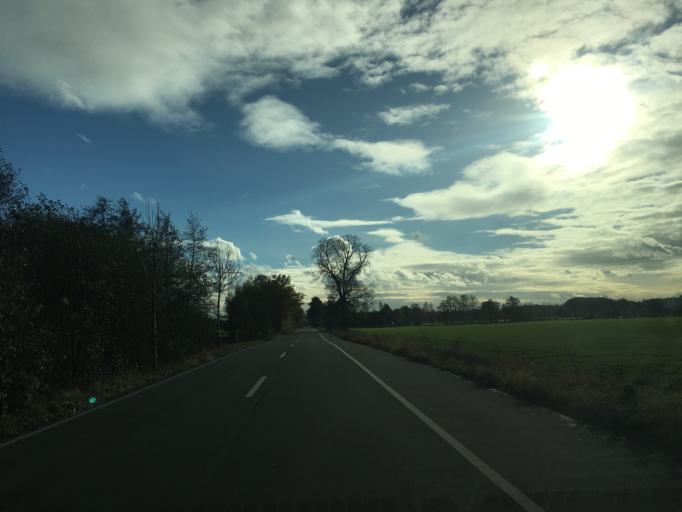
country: DE
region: North Rhine-Westphalia
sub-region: Regierungsbezirk Munster
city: Greven
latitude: 52.0333
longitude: 7.5961
